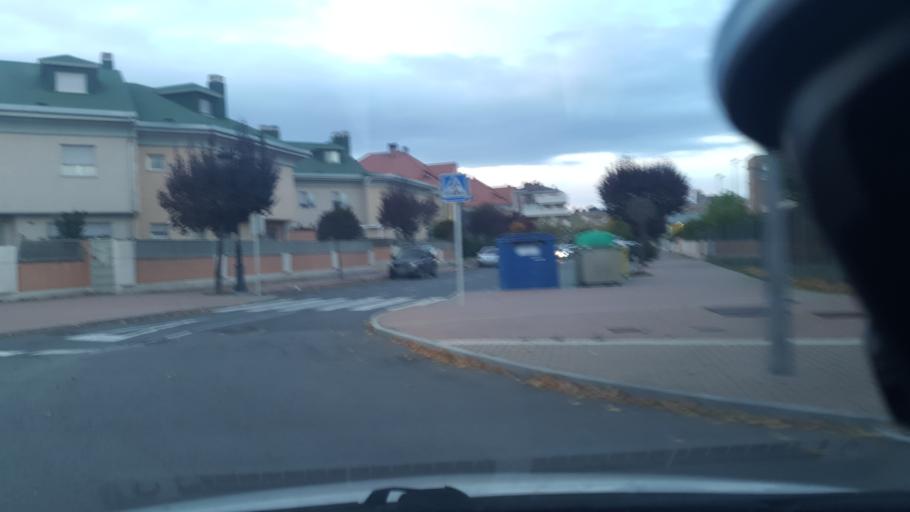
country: ES
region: Castille and Leon
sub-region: Provincia de Avila
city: Avila
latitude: 40.6416
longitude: -4.7003
